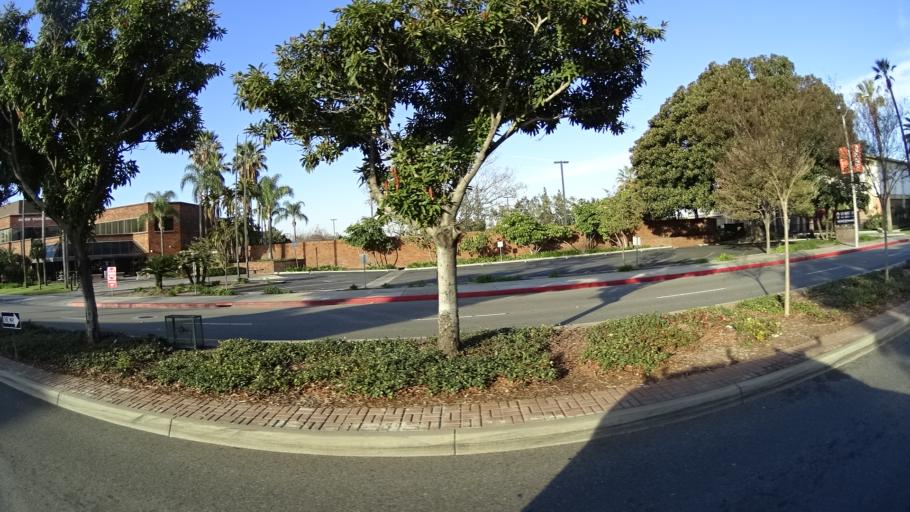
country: US
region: California
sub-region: Orange County
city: Anaheim
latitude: 33.8309
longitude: -117.9188
